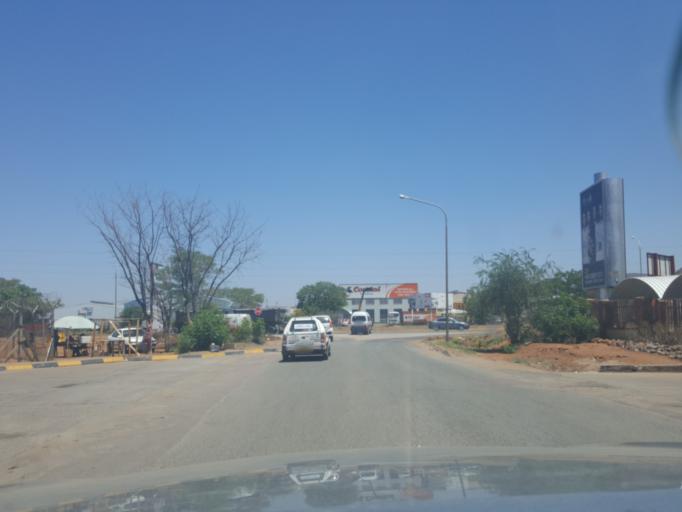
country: BW
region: South East
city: Gaborone
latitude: -24.6887
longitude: 25.8865
